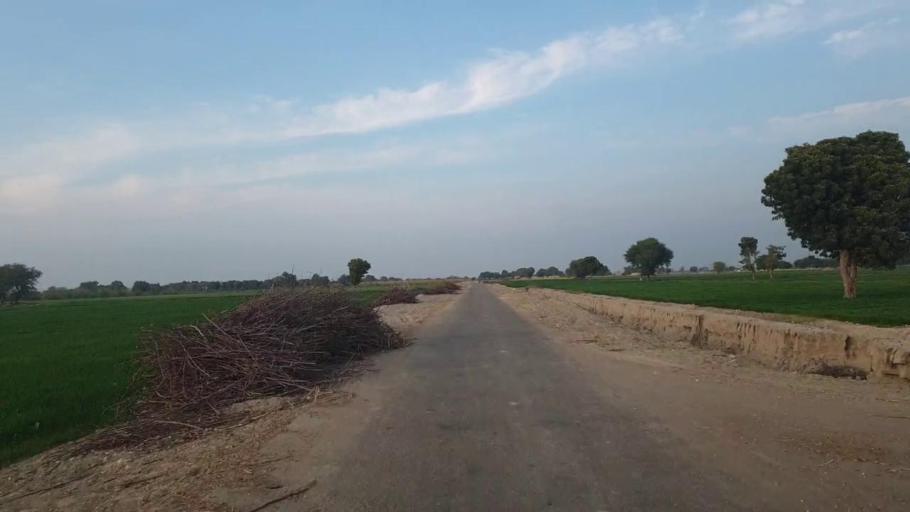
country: PK
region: Sindh
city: Shahpur Chakar
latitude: 26.1035
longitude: 68.5465
